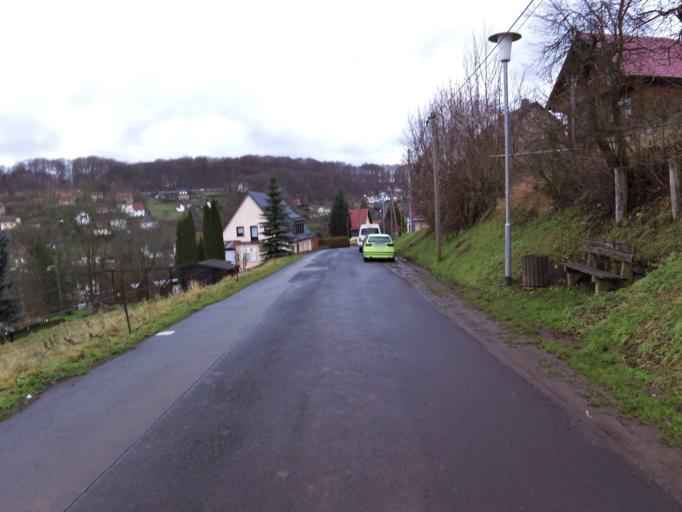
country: DE
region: Thuringia
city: Steinbach
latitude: 50.8314
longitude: 10.3666
